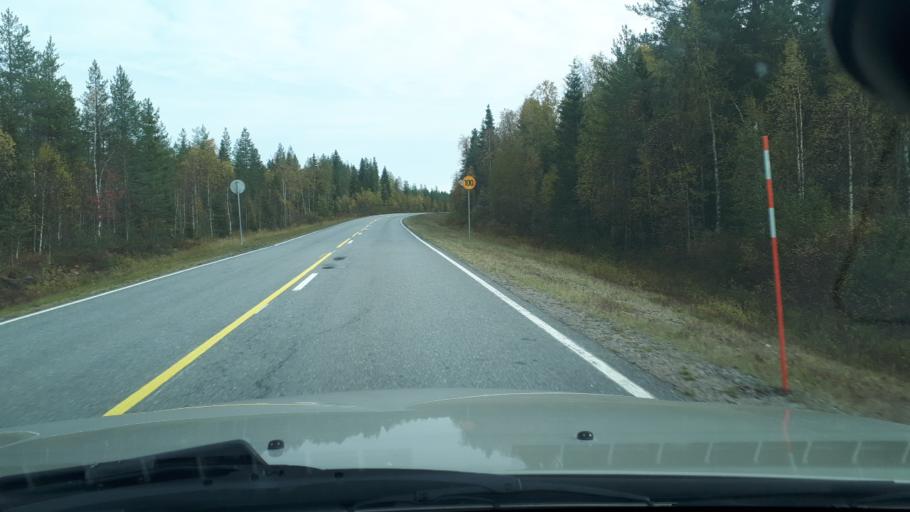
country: FI
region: Lapland
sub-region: Rovaniemi
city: Ranua
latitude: 66.0017
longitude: 26.2458
